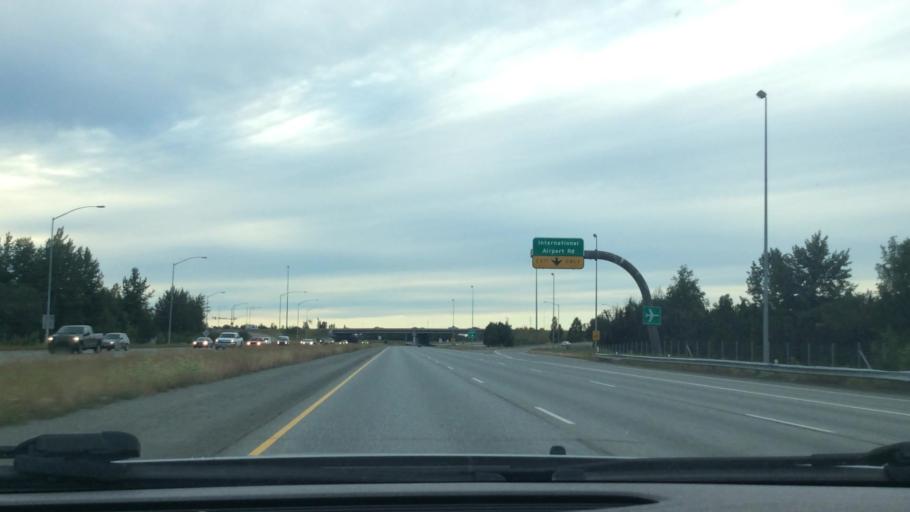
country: US
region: Alaska
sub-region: Anchorage Municipality
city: Anchorage
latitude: 61.1680
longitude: -149.9157
